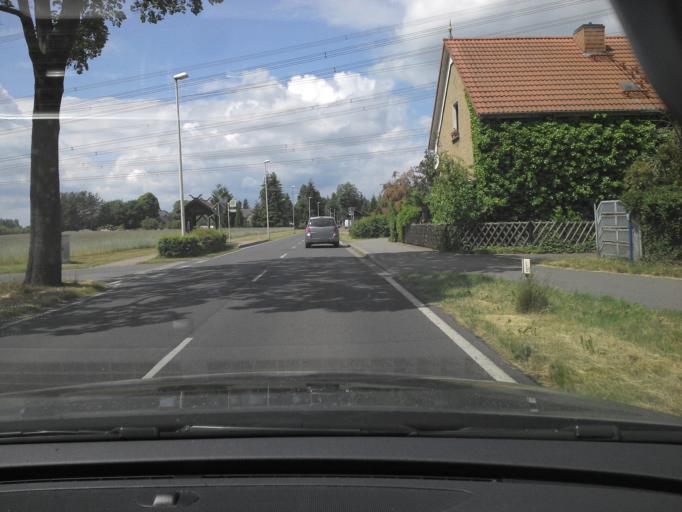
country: DE
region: Brandenburg
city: Werben
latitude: 51.8102
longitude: 14.2017
